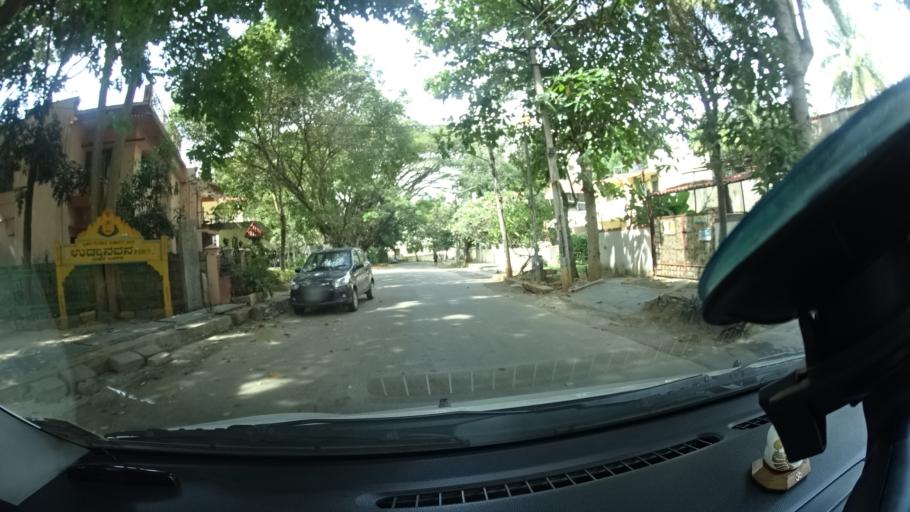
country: IN
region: Karnataka
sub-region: Bangalore Urban
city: Yelahanka
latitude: 13.1009
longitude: 77.5732
